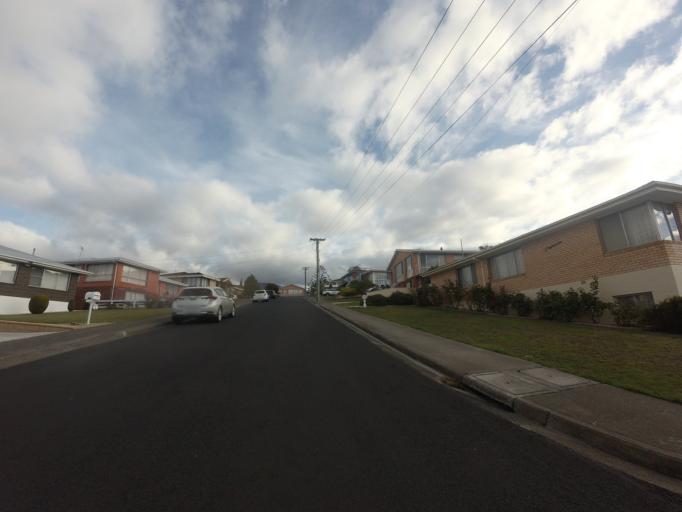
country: AU
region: Tasmania
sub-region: Glenorchy
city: Glenorchy
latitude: -42.8302
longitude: 147.2605
